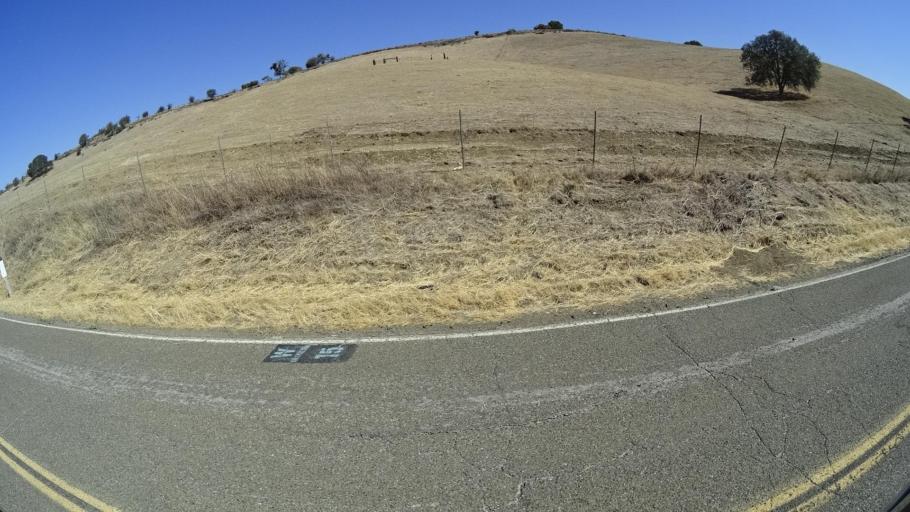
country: US
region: California
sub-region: San Luis Obispo County
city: Lake Nacimiento
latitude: 35.8469
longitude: -121.0493
